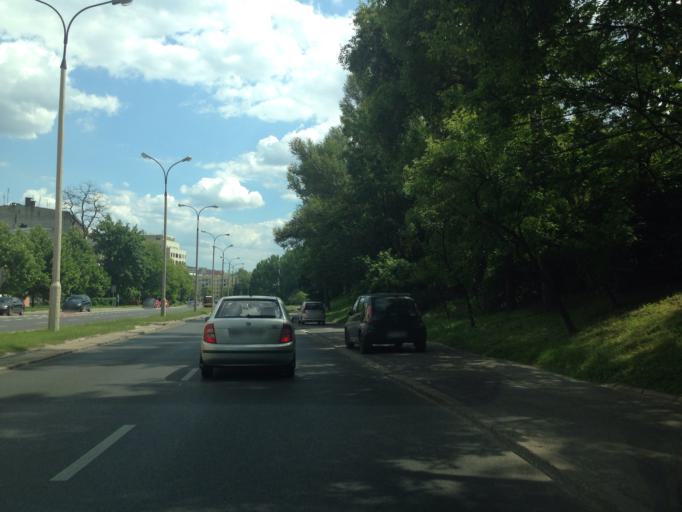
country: PL
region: Masovian Voivodeship
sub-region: Warszawa
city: Mokotow
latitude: 52.2094
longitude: 21.0258
